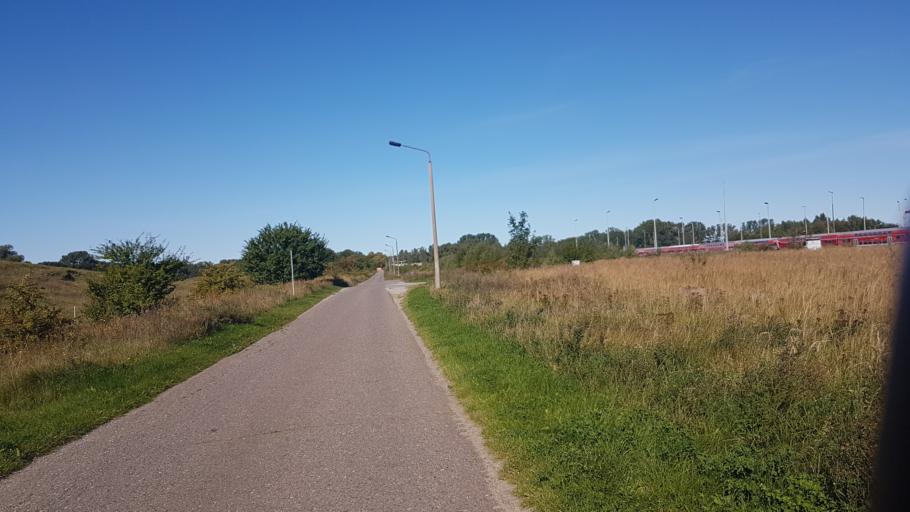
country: DE
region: Mecklenburg-Vorpommern
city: Sagard
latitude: 54.4987
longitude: 13.5435
